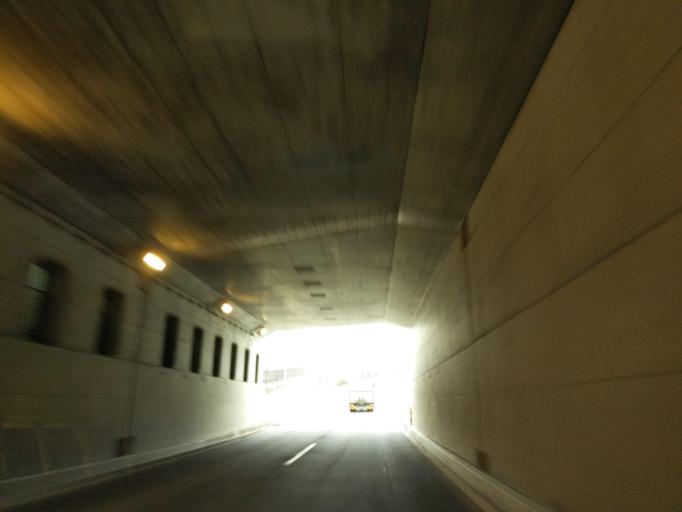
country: JP
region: Hokkaido
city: Ishikari
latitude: 43.1514
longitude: 141.3689
